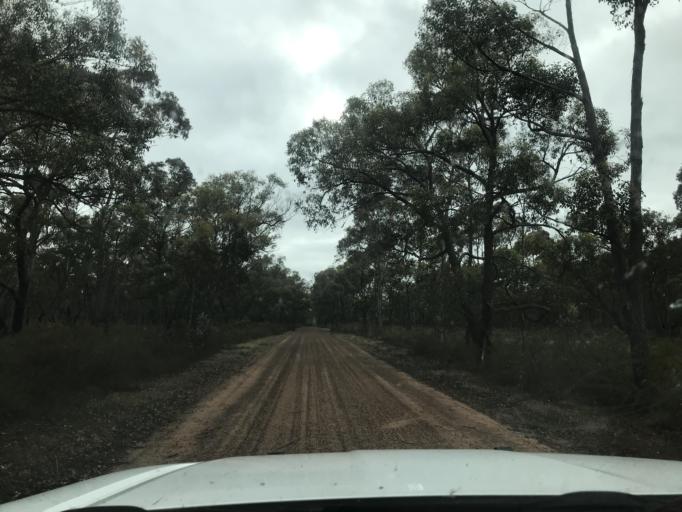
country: AU
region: South Australia
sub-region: Wattle Range
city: Penola
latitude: -37.1180
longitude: 141.1284
